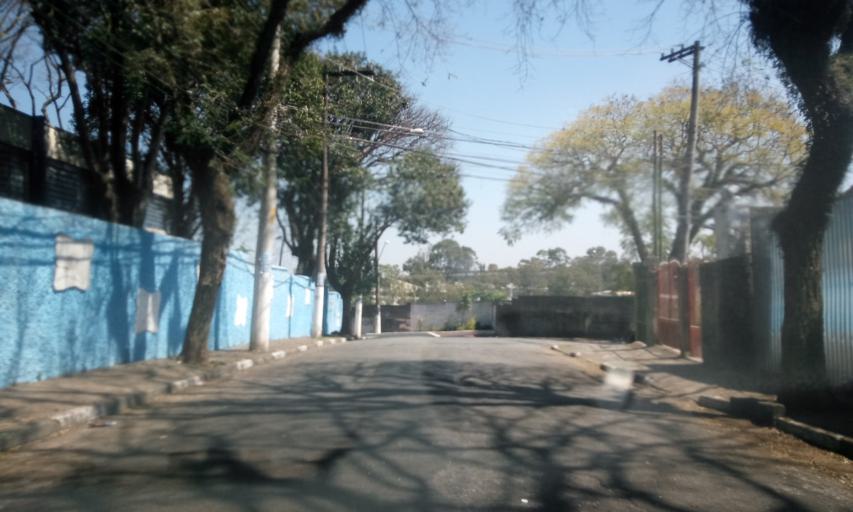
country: BR
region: Sao Paulo
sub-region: Sao Bernardo Do Campo
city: Sao Bernardo do Campo
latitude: -23.6946
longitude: -46.5703
